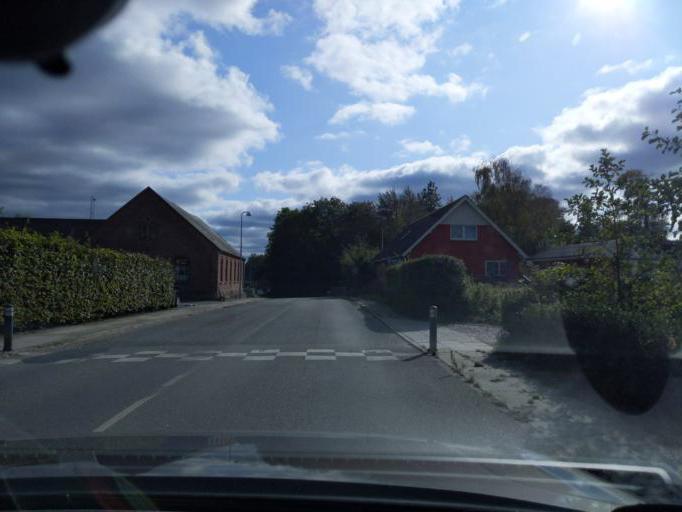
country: DK
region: North Denmark
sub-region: Mariagerfjord Kommune
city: Hobro
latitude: 56.5306
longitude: 9.7260
